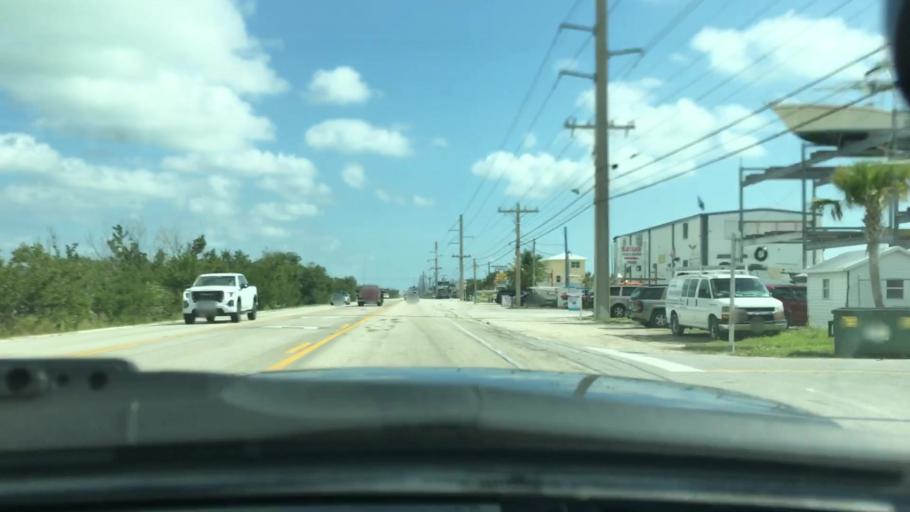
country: US
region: Florida
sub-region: Monroe County
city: Cudjoe Key
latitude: 24.6619
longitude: -81.4537
